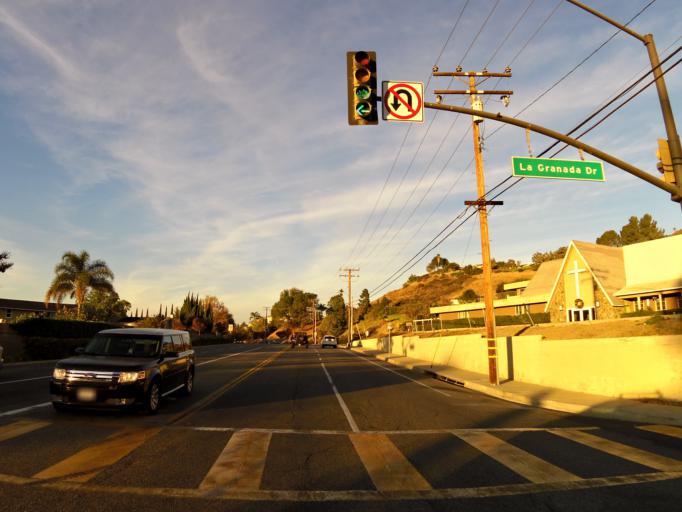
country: US
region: California
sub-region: Ventura County
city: Thousand Oaks
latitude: 34.1943
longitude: -118.8429
